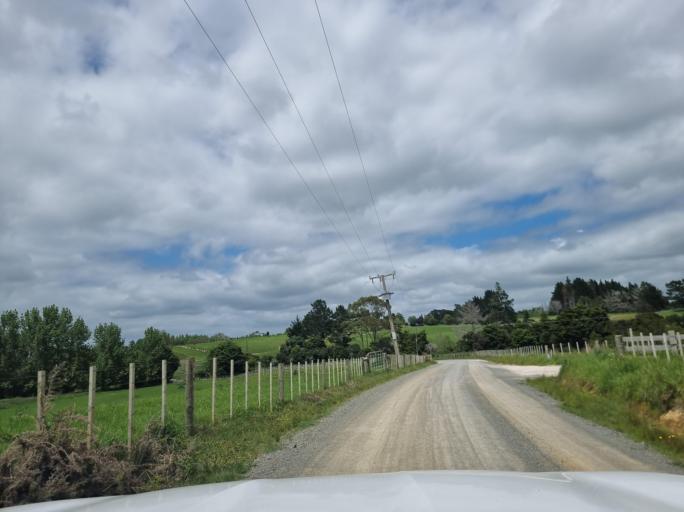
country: NZ
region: Northland
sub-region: Whangarei
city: Ruakaka
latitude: -36.0813
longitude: 174.5504
